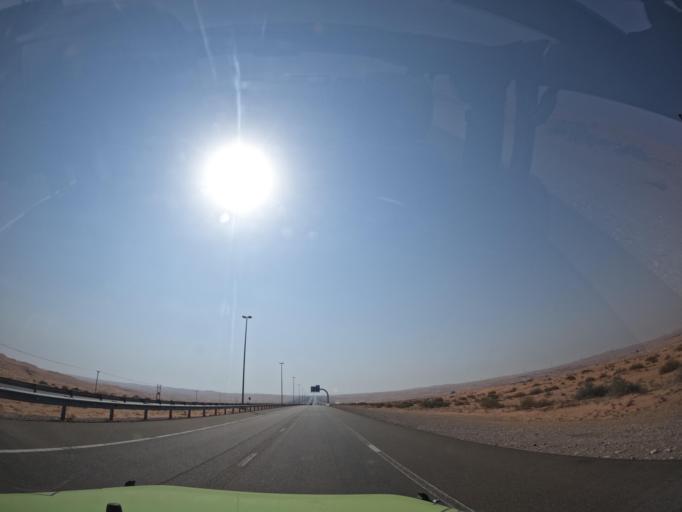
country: OM
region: Al Buraimi
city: Al Buraymi
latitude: 24.4450
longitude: 55.6596
